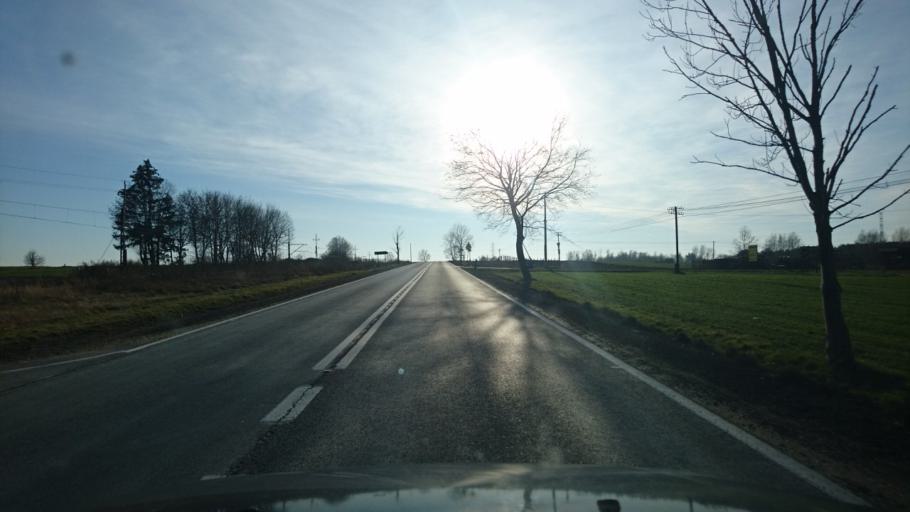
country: PL
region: Opole Voivodeship
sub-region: Powiat oleski
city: Dalachow
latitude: 51.0647
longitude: 18.6006
